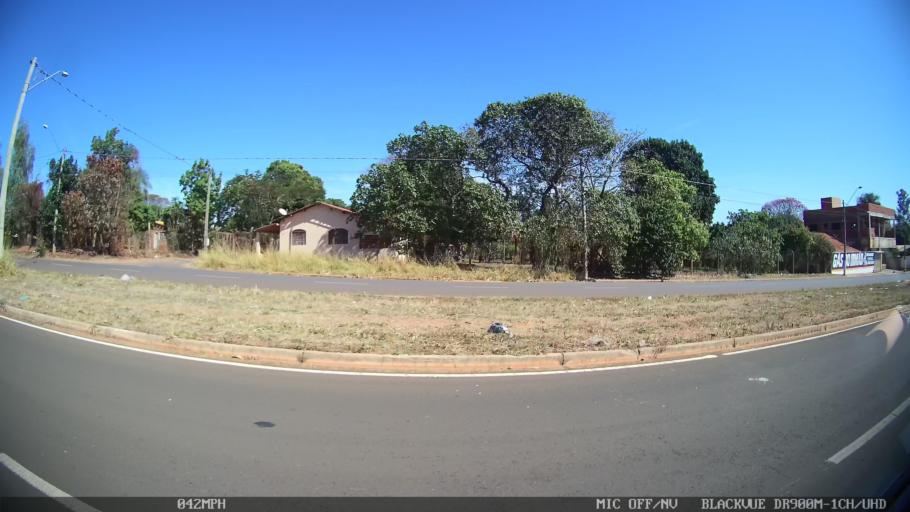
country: BR
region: Sao Paulo
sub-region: Sao Jose Do Rio Preto
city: Sao Jose do Rio Preto
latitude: -20.7288
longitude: -49.4383
